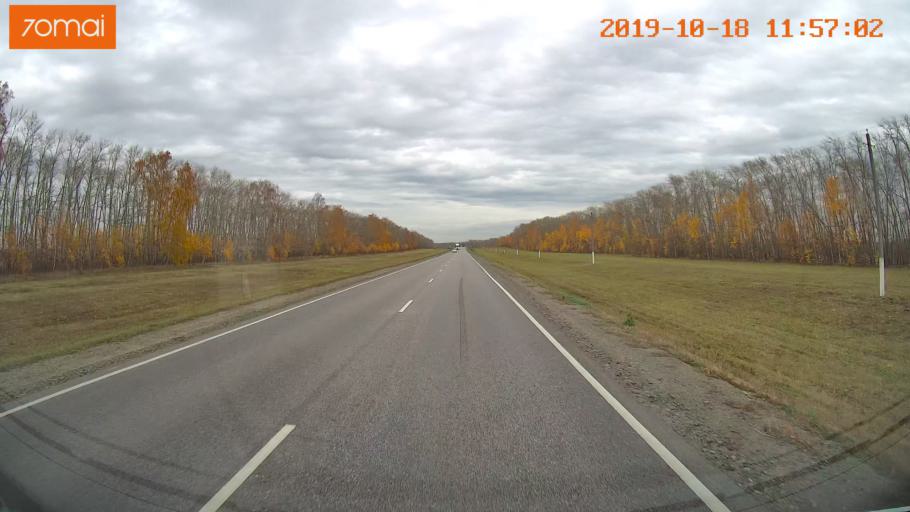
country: RU
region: Rjazan
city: Mikhaylov
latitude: 54.2661
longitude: 39.1324
